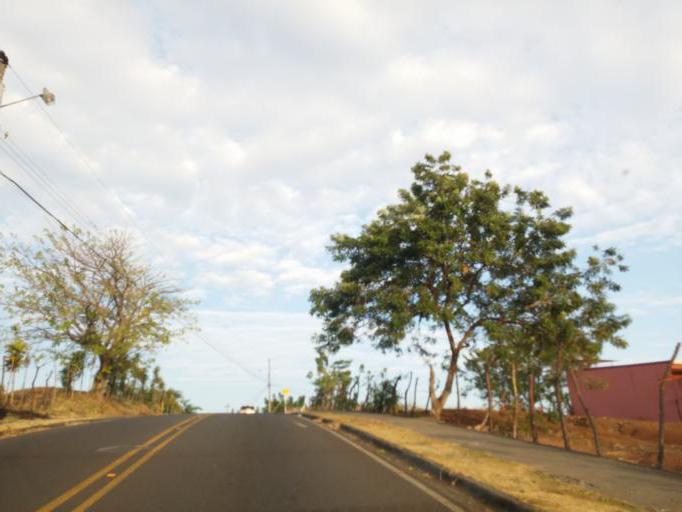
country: CR
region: Alajuela
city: Alajuela
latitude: 10.0128
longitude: -84.2192
